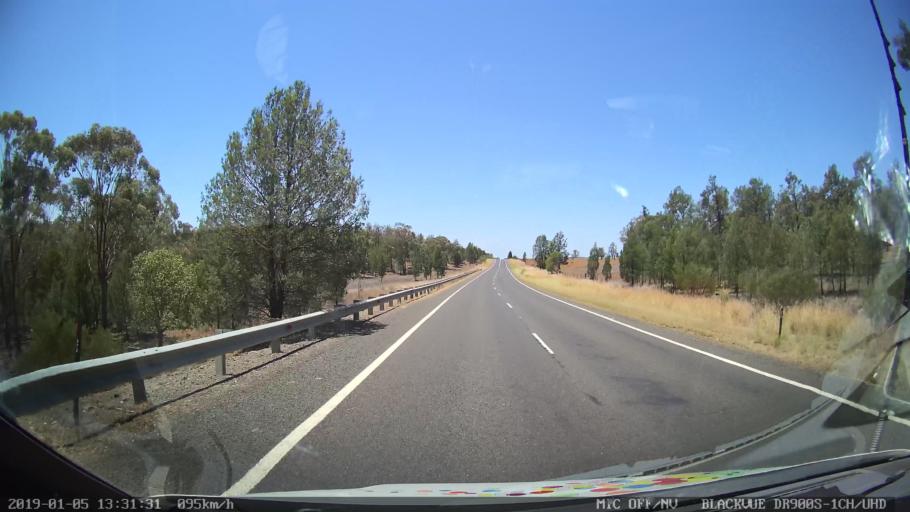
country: AU
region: New South Wales
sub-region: Gunnedah
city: Gunnedah
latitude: -31.0104
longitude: 150.0852
